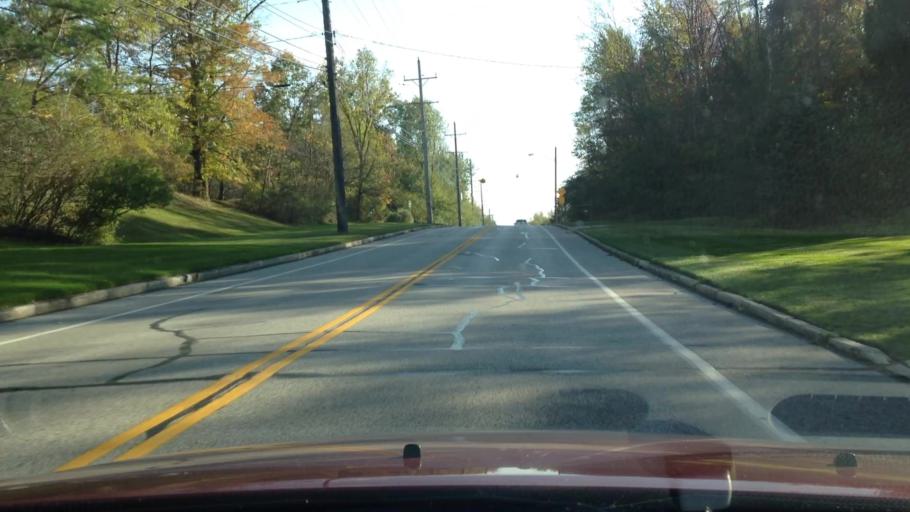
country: US
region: Ohio
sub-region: Cuyahoga County
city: Pepper Pike
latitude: 41.4743
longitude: -81.4634
